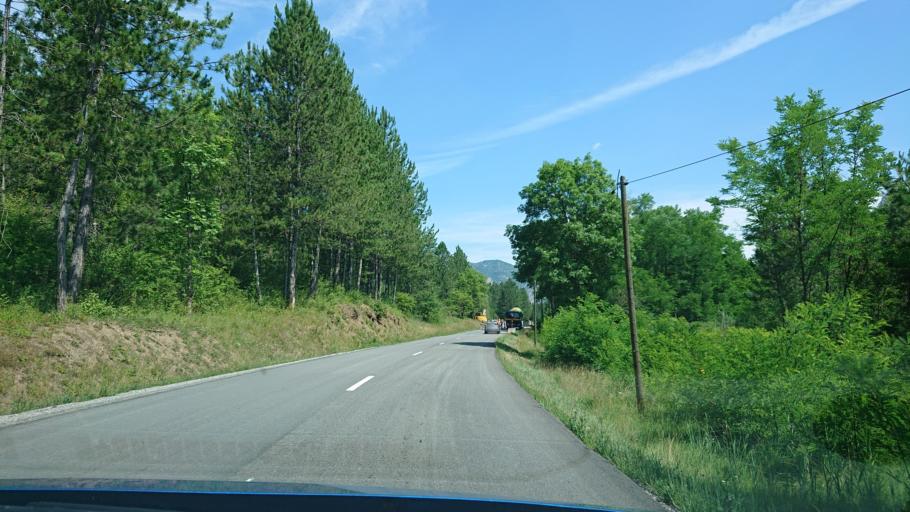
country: FR
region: Provence-Alpes-Cote d'Azur
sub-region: Departement des Hautes-Alpes
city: Tallard
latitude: 44.3198
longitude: 6.0302
